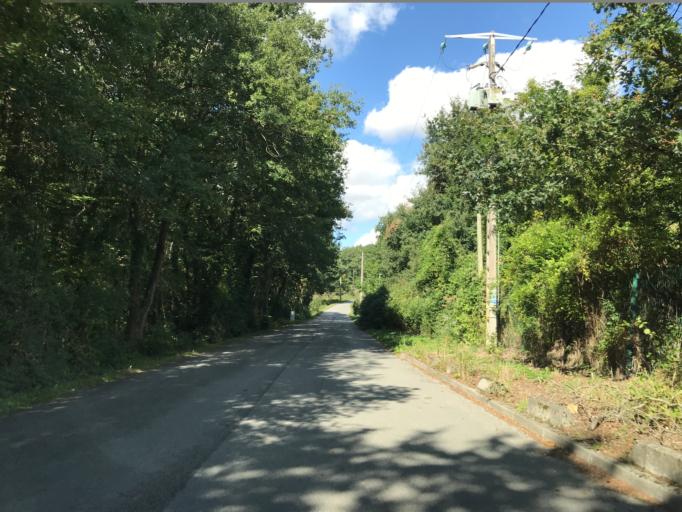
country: FR
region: Haute-Normandie
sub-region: Departement de l'Eure
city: La Chapelle-Reanville
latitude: 49.0902
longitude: 1.3955
